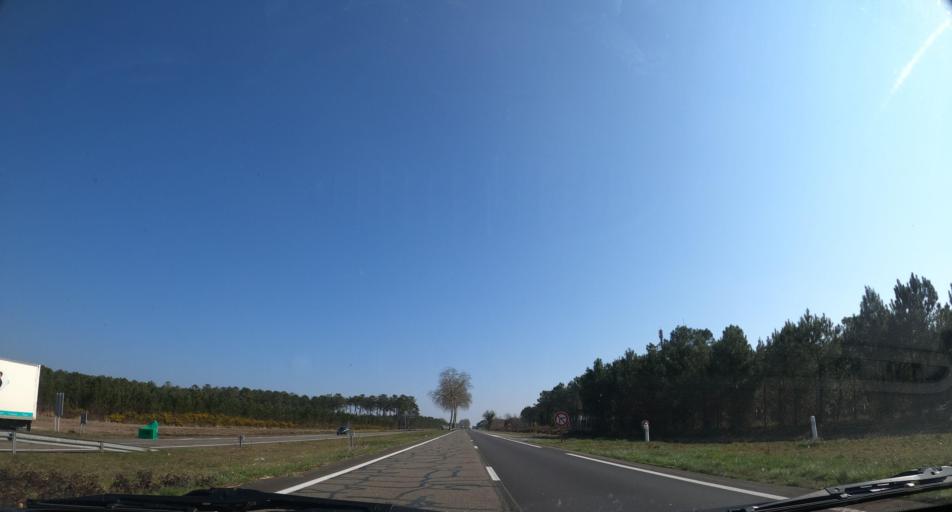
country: FR
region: Aquitaine
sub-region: Departement des Landes
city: Riviere-Saas-et-Gourby
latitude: 43.7084
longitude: -1.1622
